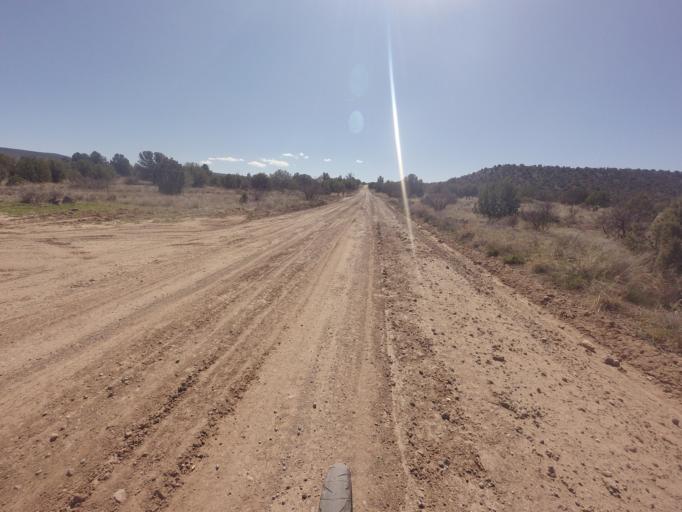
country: US
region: Arizona
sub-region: Yavapai County
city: Lake Montezuma
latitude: 34.6049
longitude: -111.7240
